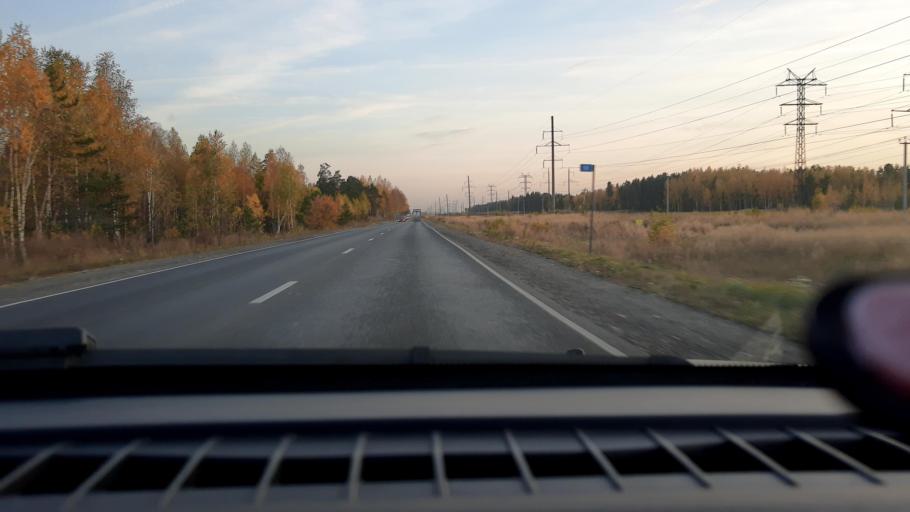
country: RU
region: Nizjnij Novgorod
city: Babino
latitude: 56.3170
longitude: 43.5592
